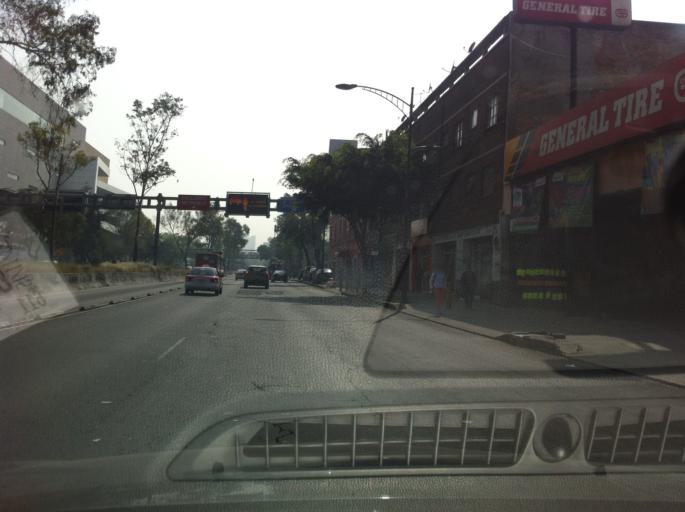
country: MX
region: Mexico City
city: Cuauhtemoc
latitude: 19.4496
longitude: -99.1526
